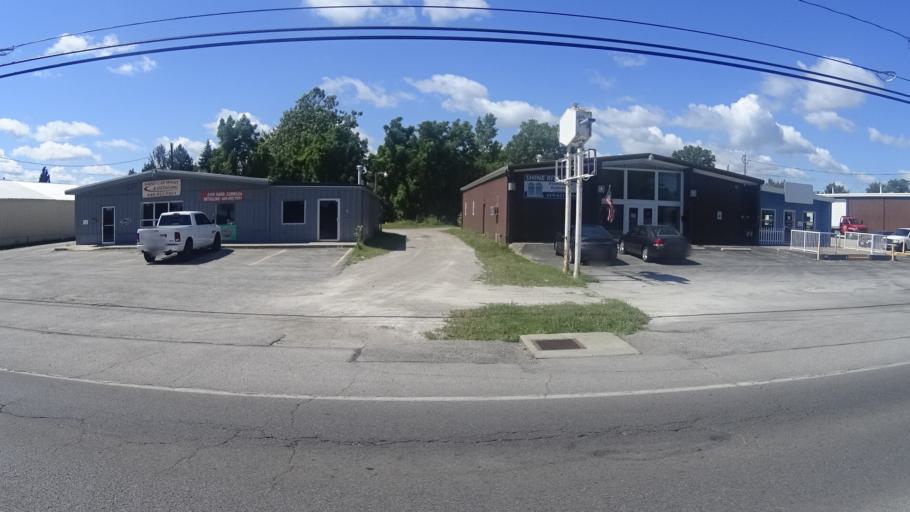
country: US
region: Ohio
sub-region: Erie County
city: Sandusky
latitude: 41.4286
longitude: -82.6675
